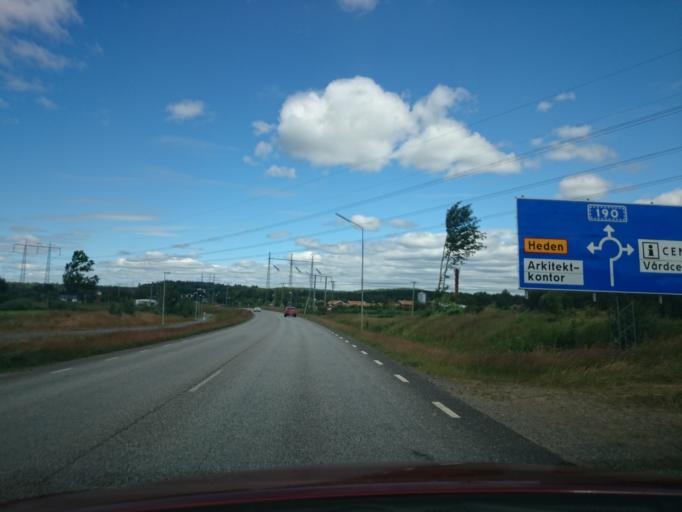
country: SE
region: Vaestra Goetaland
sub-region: Lerums Kommun
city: Grabo
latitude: 57.8325
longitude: 12.2917
